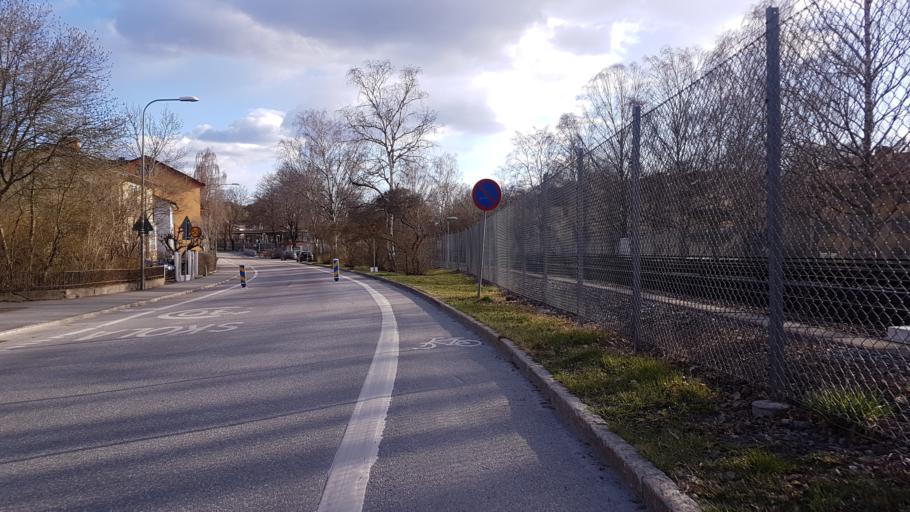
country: SE
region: Stockholm
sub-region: Stockholms Kommun
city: Arsta
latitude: 59.2911
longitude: 18.0701
